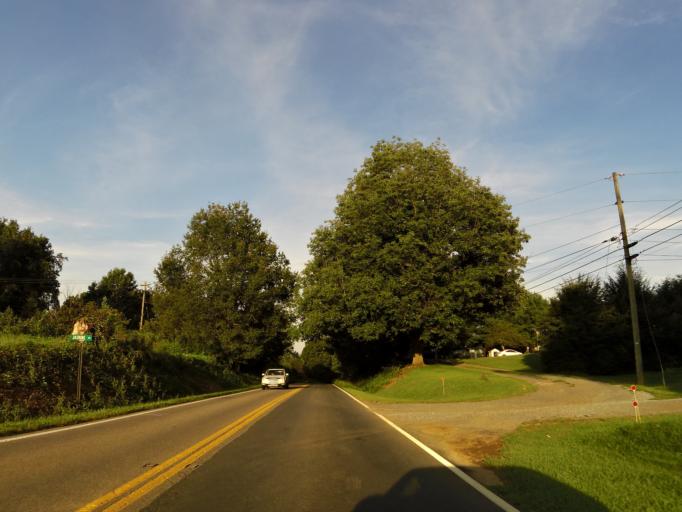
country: US
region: Virginia
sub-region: Washington County
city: Emory
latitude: 36.6502
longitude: -81.8414
